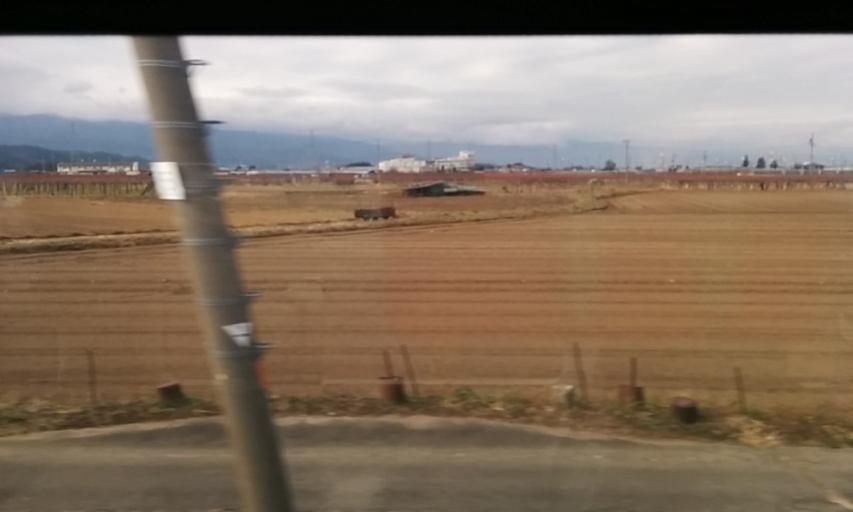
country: JP
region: Nagano
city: Shiojiri
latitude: 36.1059
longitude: 137.9391
